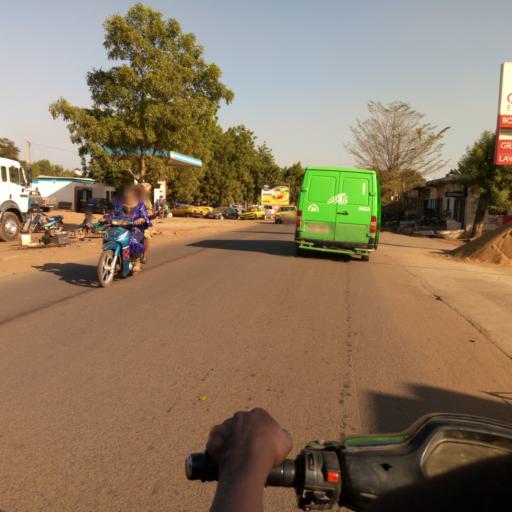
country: ML
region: Bamako
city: Bamako
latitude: 12.6540
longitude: -8.0208
